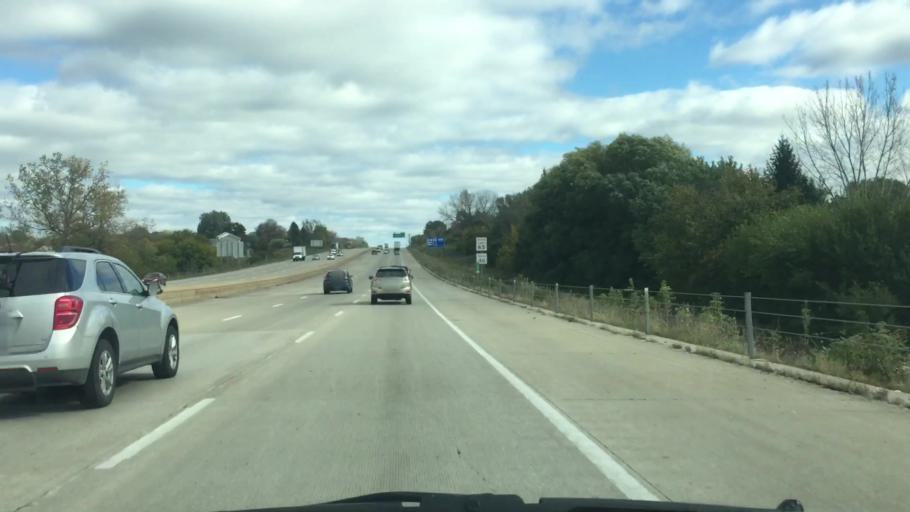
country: US
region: Iowa
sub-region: Johnson County
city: Coralville
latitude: 41.6925
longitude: -91.5952
